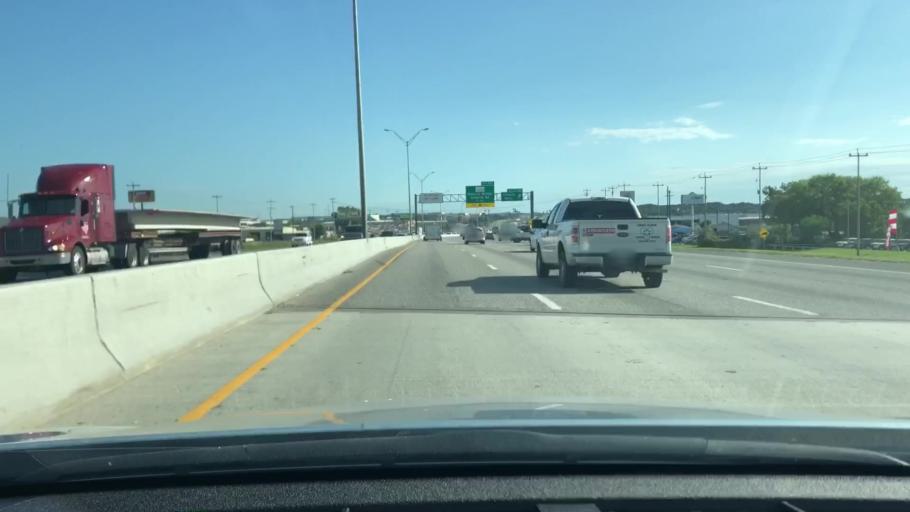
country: US
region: Texas
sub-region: Bexar County
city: Selma
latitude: 29.5865
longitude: -98.3024
